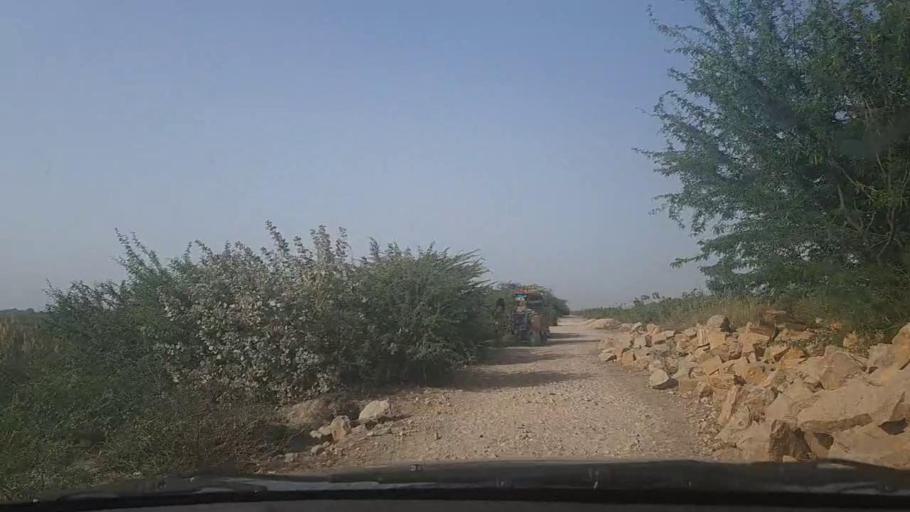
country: PK
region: Sindh
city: Keti Bandar
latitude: 24.2577
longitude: 67.5636
